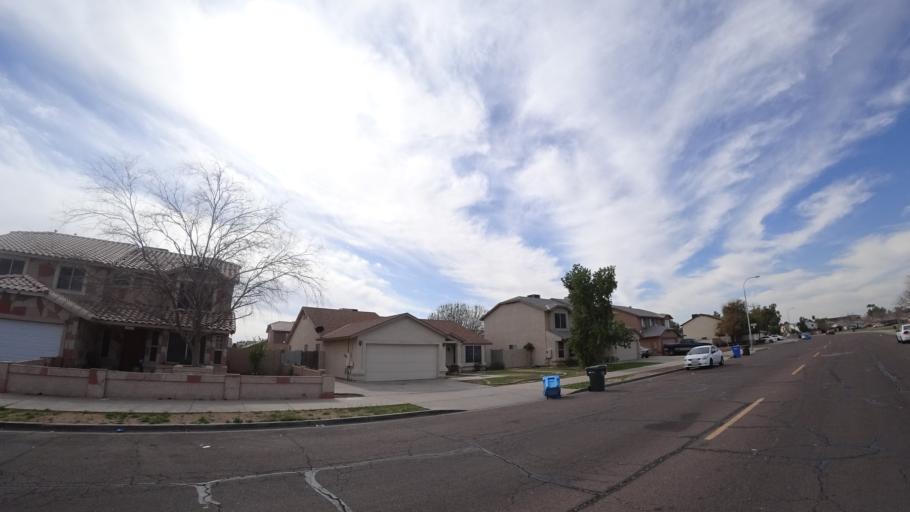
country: US
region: Arizona
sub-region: Maricopa County
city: Tolleson
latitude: 33.4718
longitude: -112.2444
